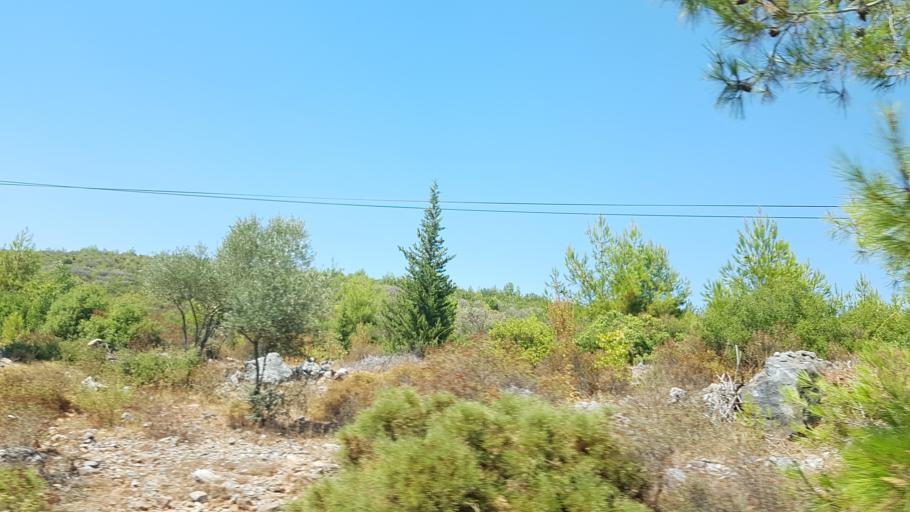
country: TR
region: Mugla
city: Karaova
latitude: 37.0466
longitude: 27.7044
